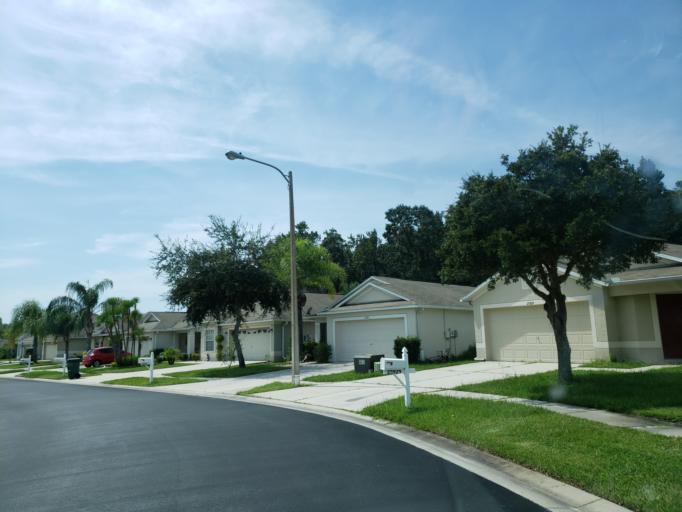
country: US
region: Florida
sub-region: Pasco County
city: Wesley Chapel
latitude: 28.2232
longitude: -82.3870
